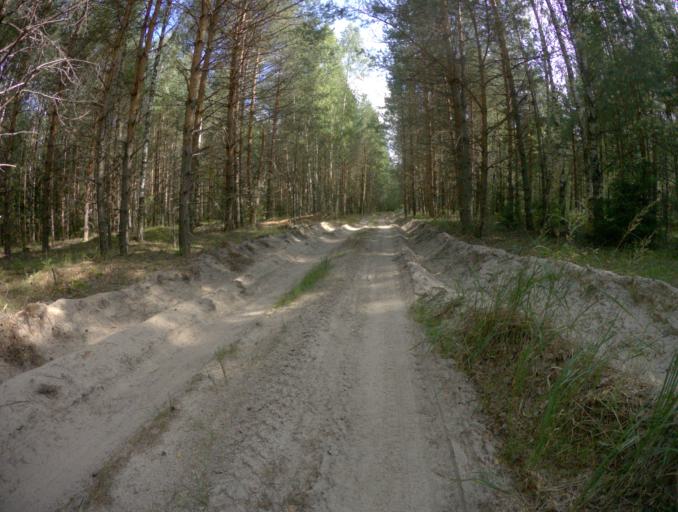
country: RU
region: Vladimir
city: Vorsha
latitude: 55.9050
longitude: 40.1718
